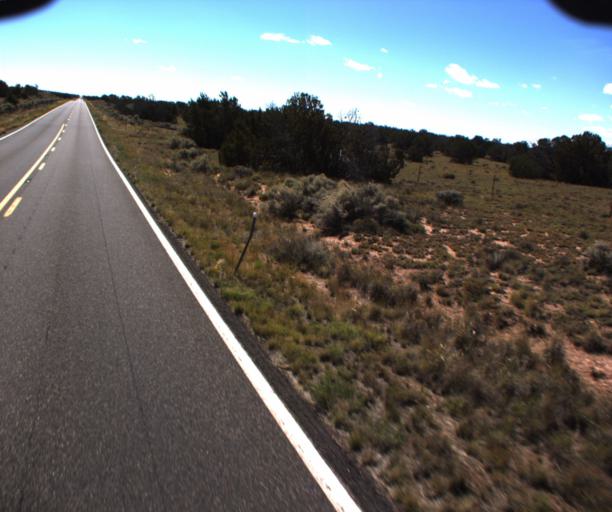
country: US
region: Arizona
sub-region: Apache County
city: Saint Johns
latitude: 34.8814
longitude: -109.2379
